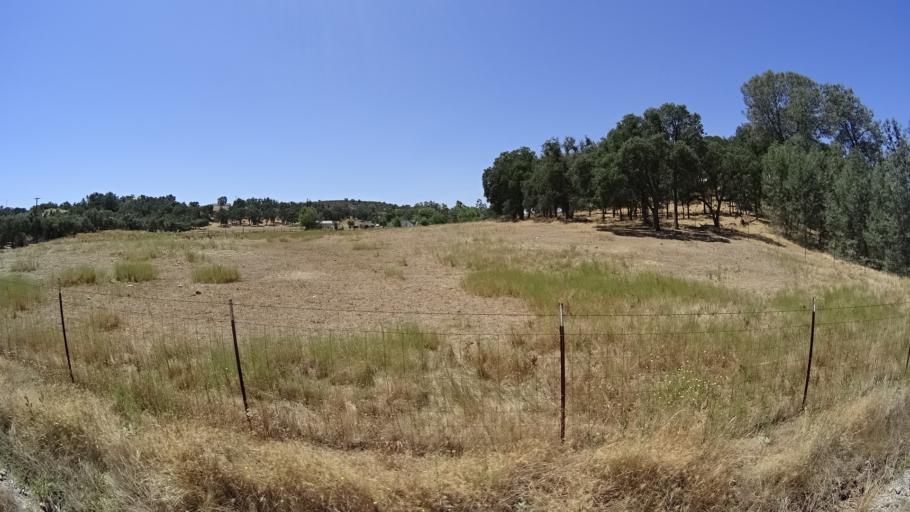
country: US
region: California
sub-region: Calaveras County
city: Rancho Calaveras
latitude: 38.1399
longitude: -120.8913
